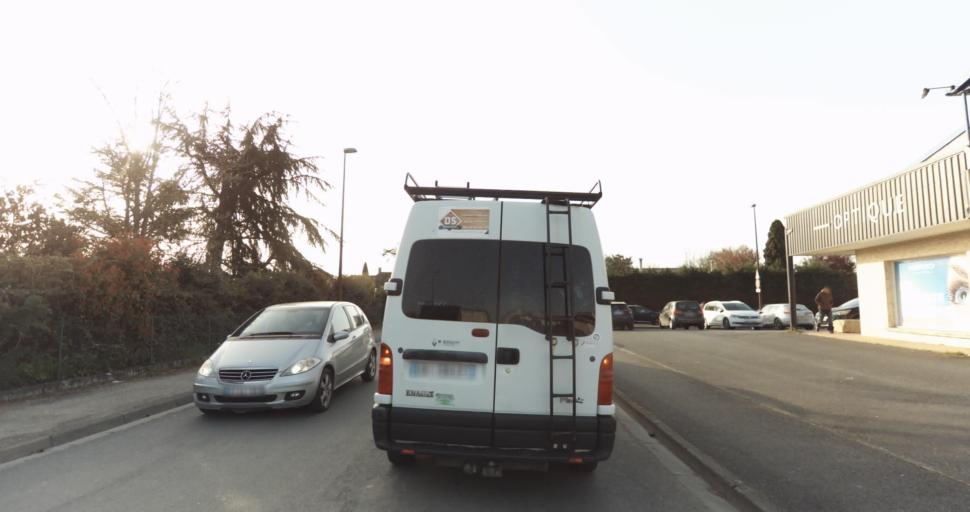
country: FR
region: Midi-Pyrenees
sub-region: Departement du Tarn
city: Saint-Sulpice-la-Pointe
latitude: 43.7722
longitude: 1.6775
